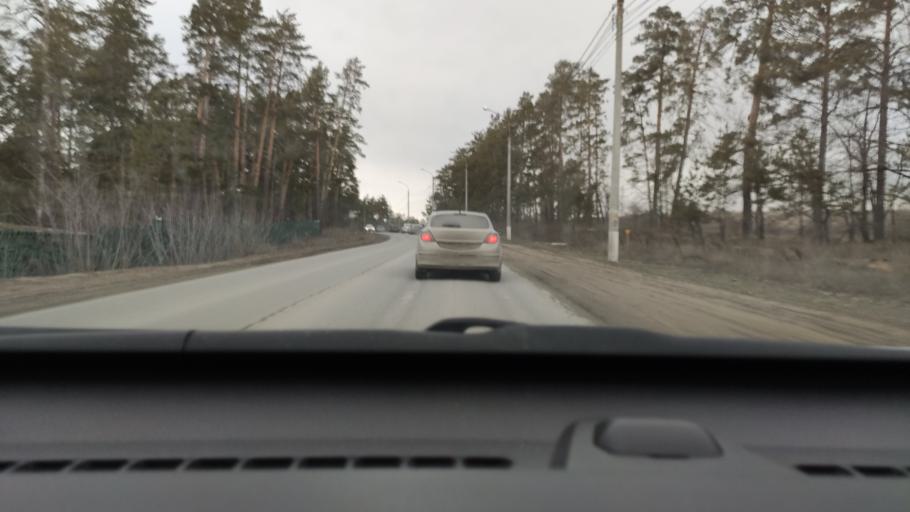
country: RU
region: Samara
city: Tol'yatti
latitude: 53.4842
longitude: 49.3295
